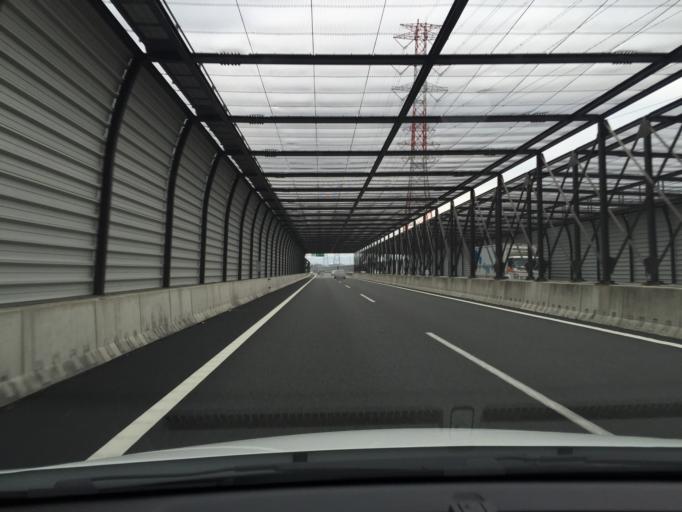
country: JP
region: Saitama
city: Sakado
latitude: 35.9757
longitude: 139.4553
